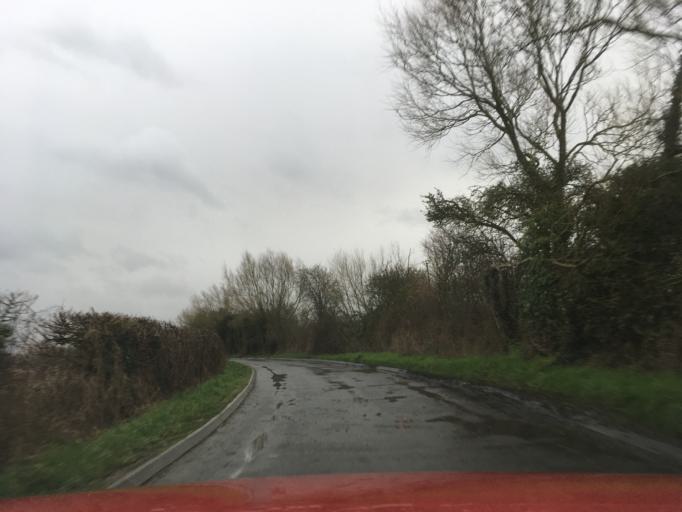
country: GB
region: England
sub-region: Oxfordshire
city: Oxford
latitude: 51.7590
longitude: -1.2857
